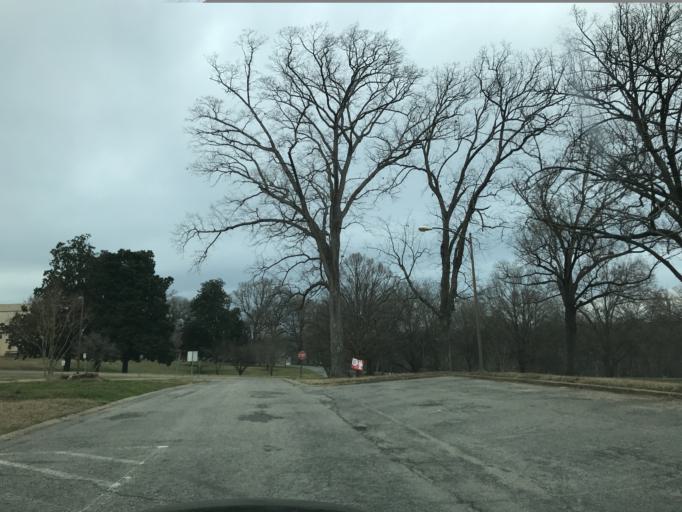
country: US
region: North Carolina
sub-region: Wake County
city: Raleigh
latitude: 35.7682
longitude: -78.6535
